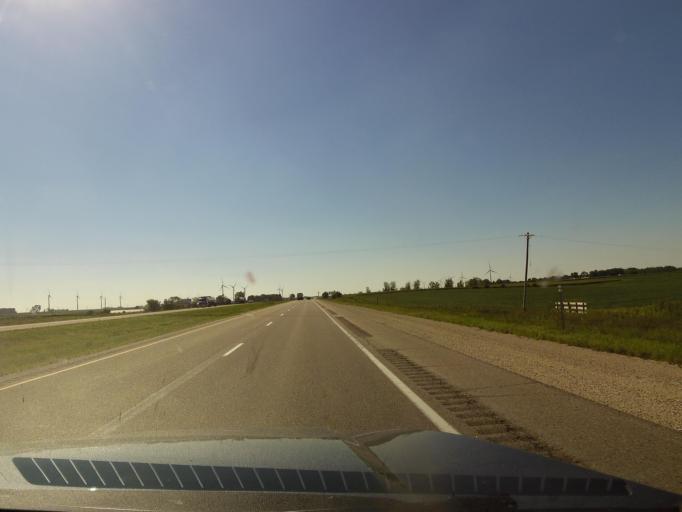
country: US
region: Iowa
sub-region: Floyd County
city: Charles City
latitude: 43.0389
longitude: -92.6815
